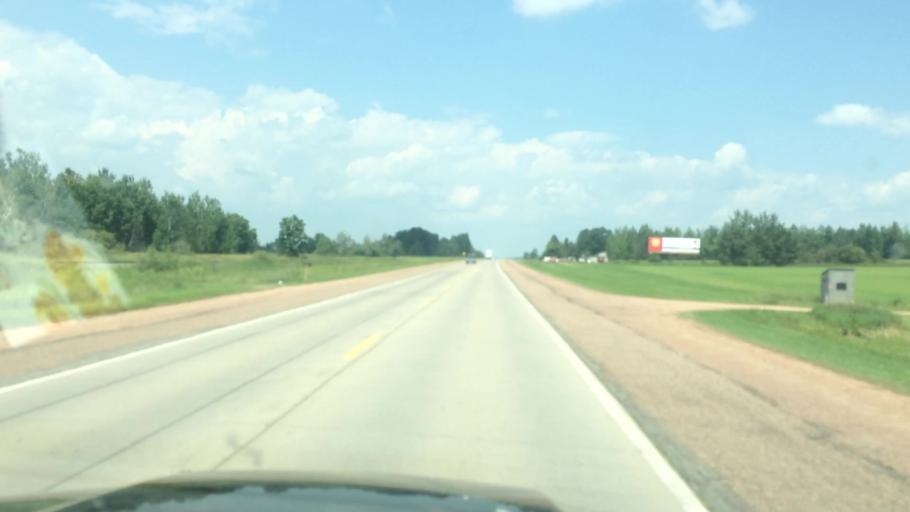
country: US
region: Wisconsin
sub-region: Clark County
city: Colby
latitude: 44.8760
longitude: -90.3157
